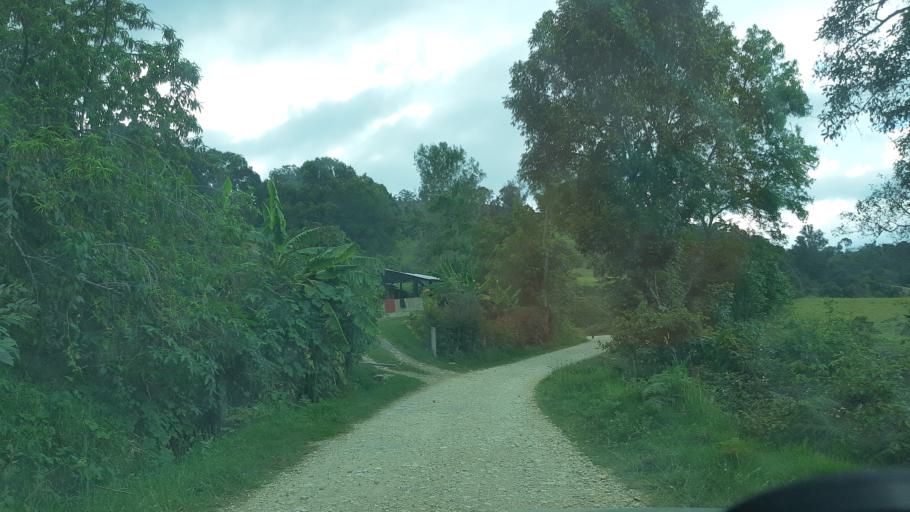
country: CO
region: Boyaca
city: Santa Sofia
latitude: 5.7479
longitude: -73.5522
